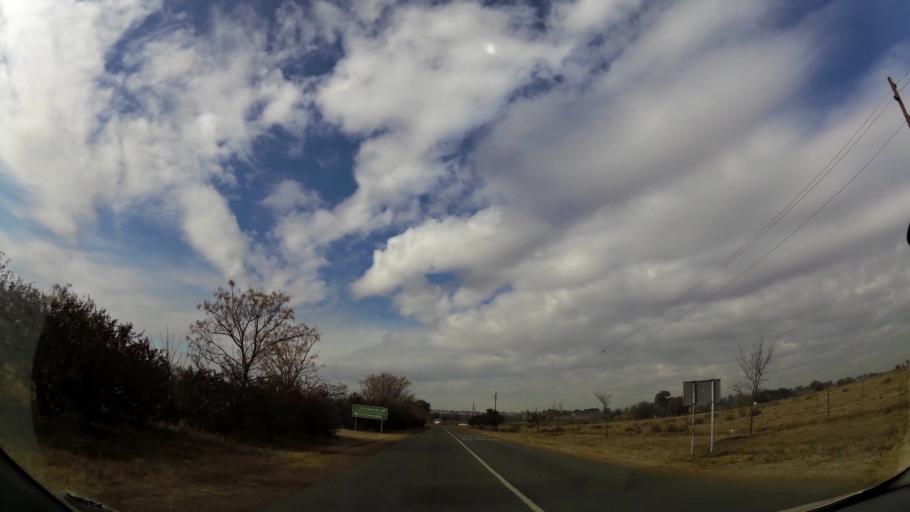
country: ZA
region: Gauteng
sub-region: Sedibeng District Municipality
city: Meyerton
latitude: -26.5553
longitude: 28.0615
